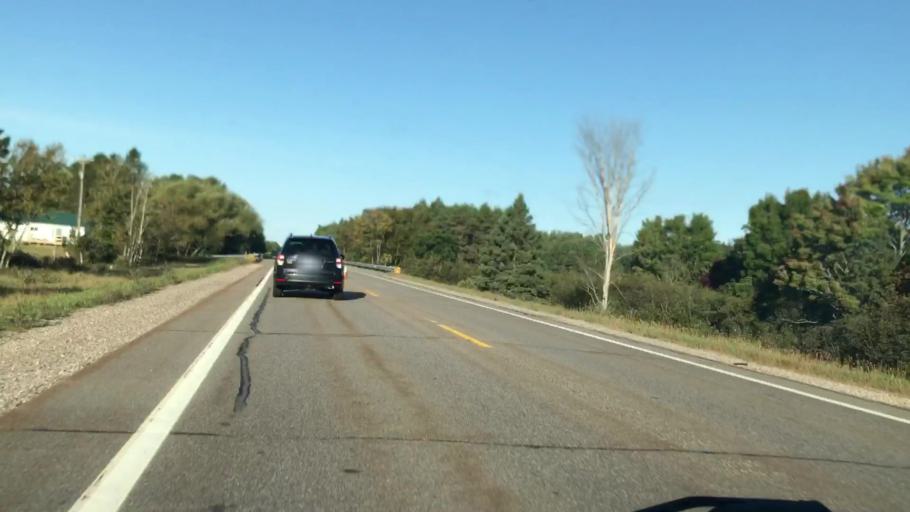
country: US
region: Michigan
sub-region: Chippewa County
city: Sault Ste. Marie
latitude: 46.3754
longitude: -84.6029
